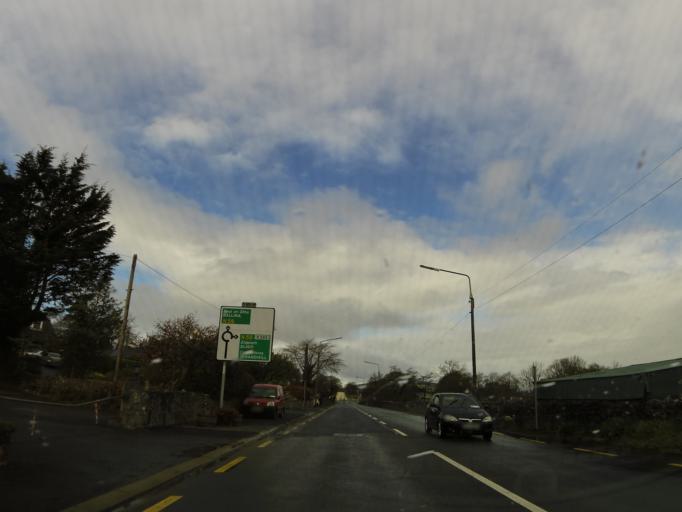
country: IE
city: Ballisodare
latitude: 54.2074
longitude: -8.5066
